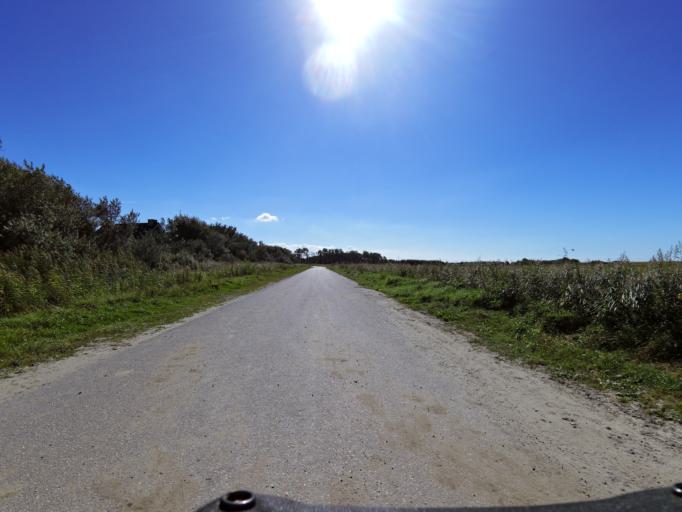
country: NL
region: South Holland
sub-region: Gemeente Goeree-Overflakkee
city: Ouddorp
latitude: 51.8231
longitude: 3.9018
